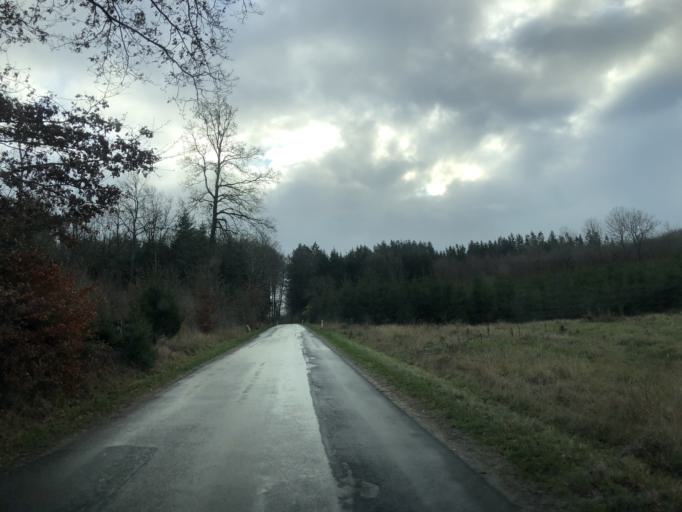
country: DK
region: North Denmark
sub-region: Rebild Kommune
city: Stovring
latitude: 56.9271
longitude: 9.8047
